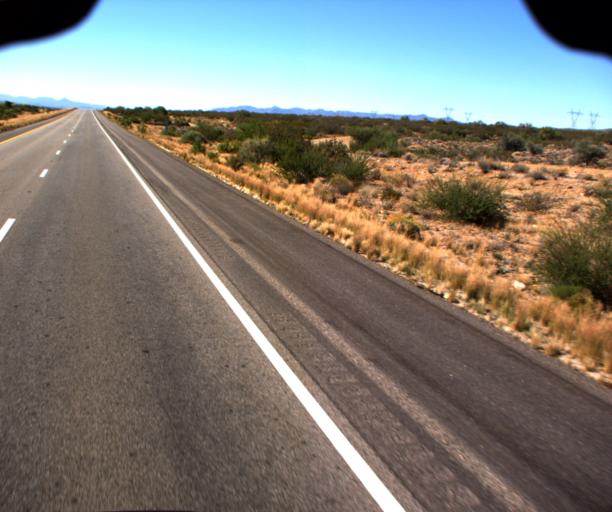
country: US
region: Arizona
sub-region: Mohave County
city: Kingman
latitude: 34.8843
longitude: -113.6496
